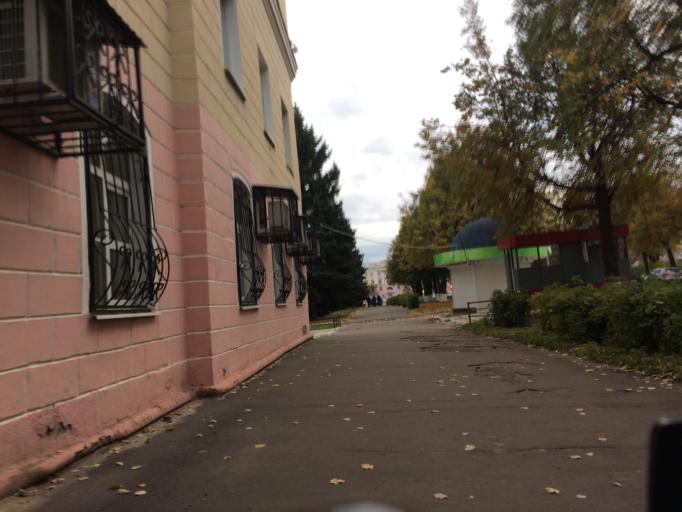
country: RU
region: Mariy-El
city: Yoshkar-Ola
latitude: 56.6327
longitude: 47.8913
